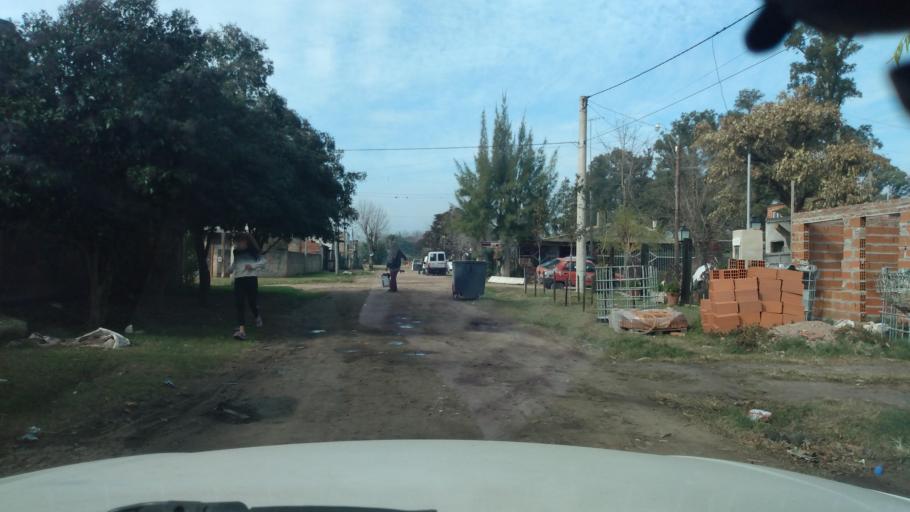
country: AR
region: Buenos Aires
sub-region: Partido de Lujan
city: Lujan
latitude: -34.5827
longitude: -59.1299
